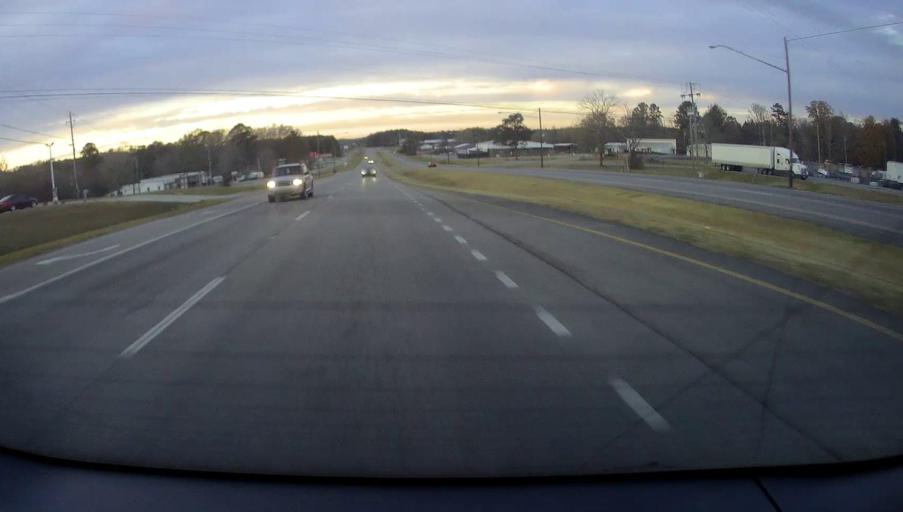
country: US
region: Alabama
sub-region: Etowah County
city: Glencoe
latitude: 33.9741
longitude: -85.9515
